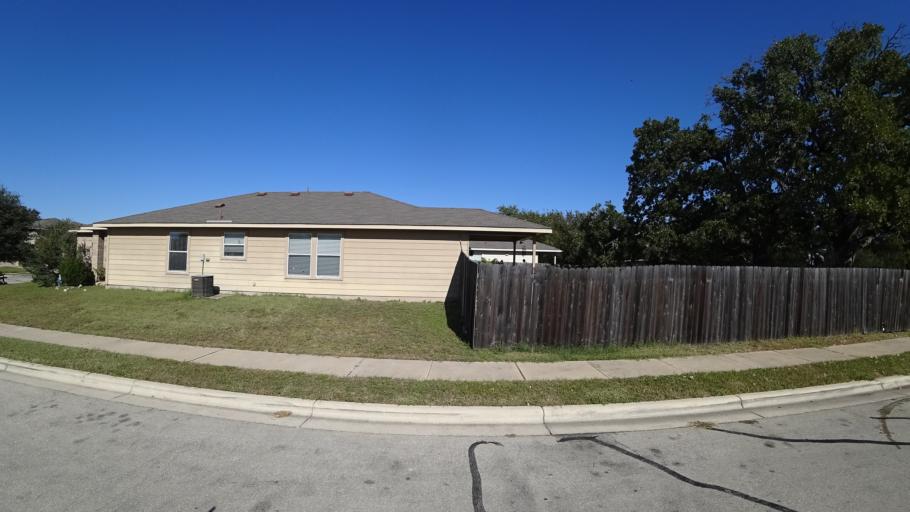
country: US
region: Texas
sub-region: Travis County
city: Hornsby Bend
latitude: 30.2822
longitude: -97.6273
